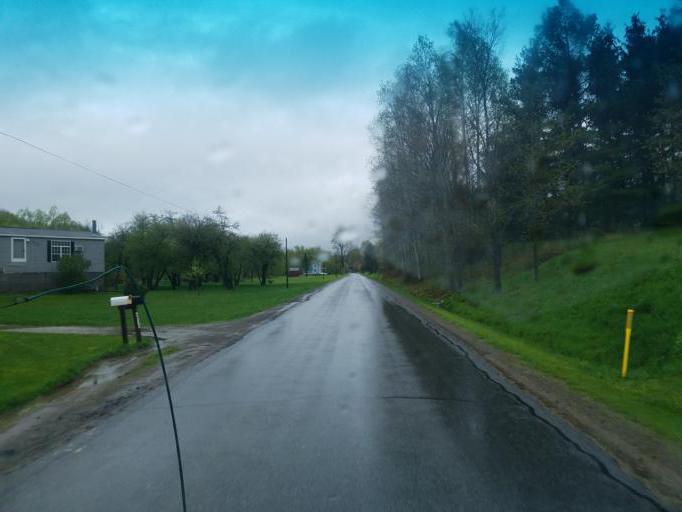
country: US
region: Pennsylvania
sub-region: Tioga County
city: Westfield
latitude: 41.9499
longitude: -77.6474
